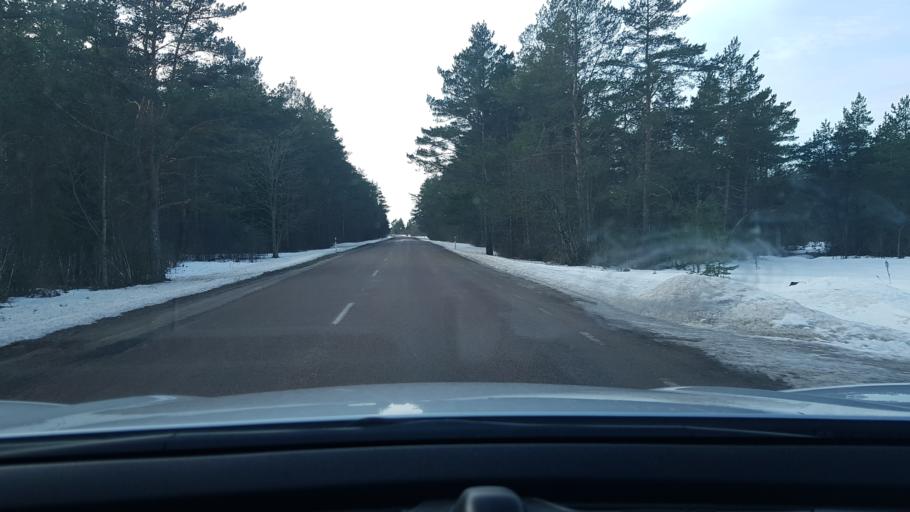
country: EE
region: Saare
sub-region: Kuressaare linn
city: Kuressaare
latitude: 58.3426
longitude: 22.5796
